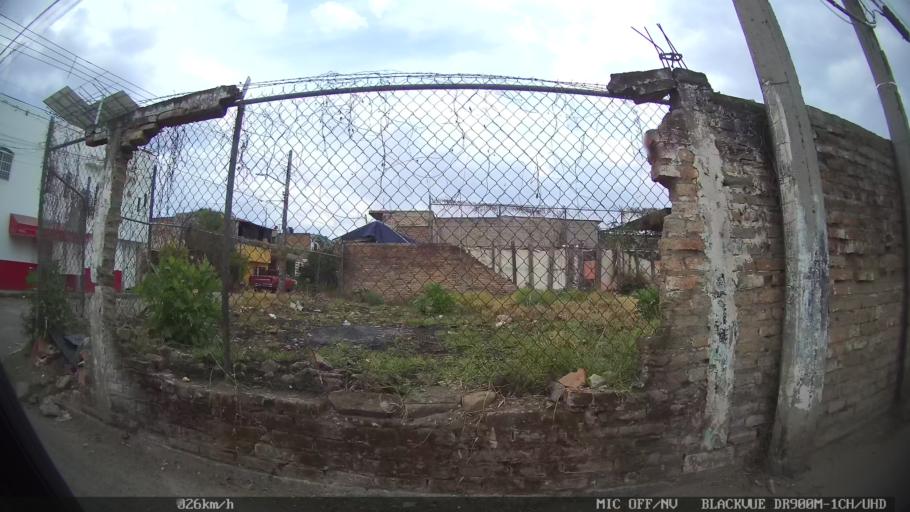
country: MX
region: Jalisco
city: Tlaquepaque
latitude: 20.6217
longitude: -103.2674
